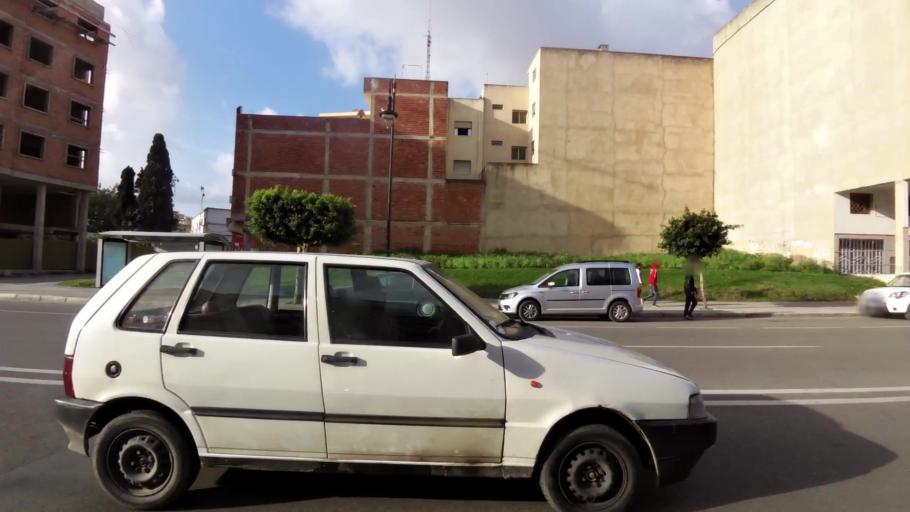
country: MA
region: Tanger-Tetouan
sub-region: Tanger-Assilah
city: Tangier
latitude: 35.7593
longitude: -5.8296
